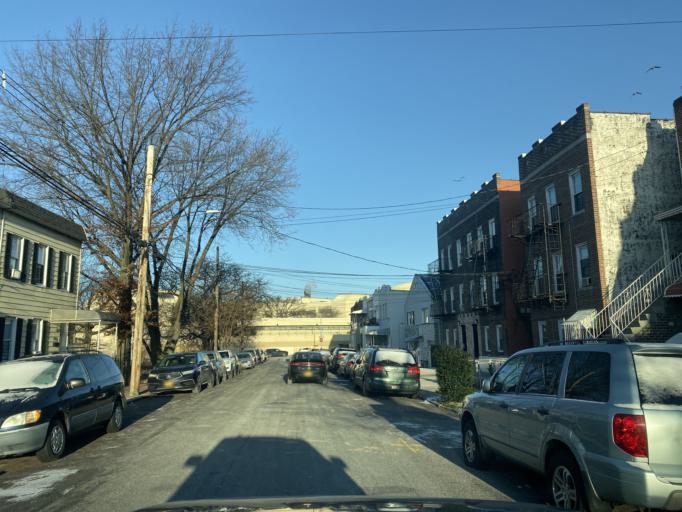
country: US
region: New York
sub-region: Bronx
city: The Bronx
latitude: 40.8388
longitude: -73.8371
